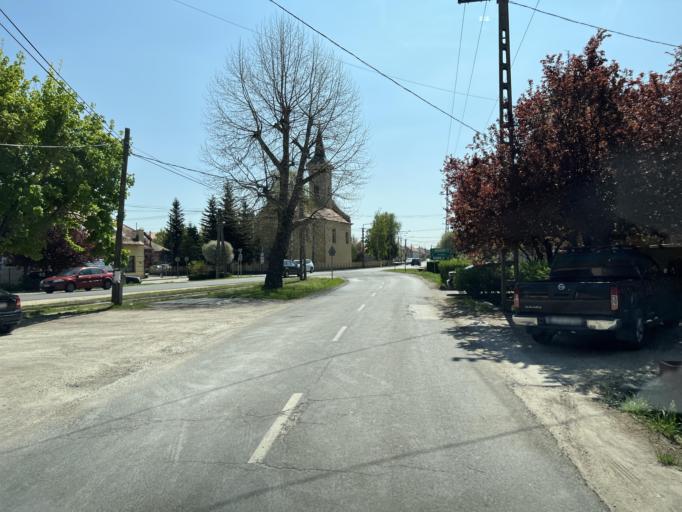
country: HU
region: Pest
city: Ocsa
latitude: 47.2941
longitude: 19.2251
